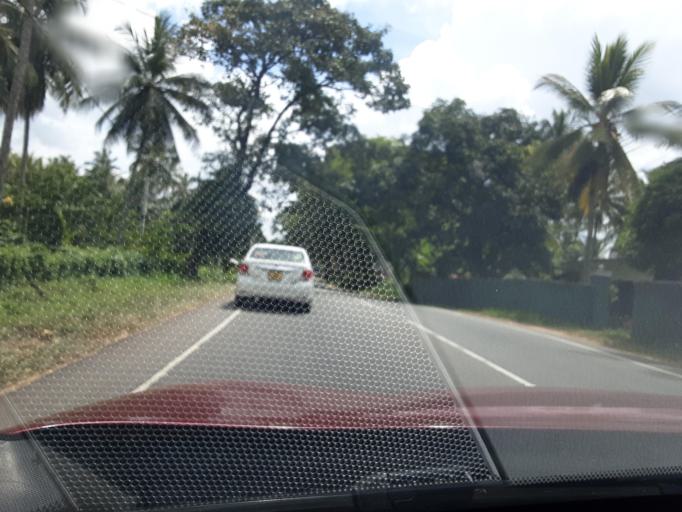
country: LK
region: North Western
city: Kurunegala
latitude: 7.4520
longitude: 80.2733
